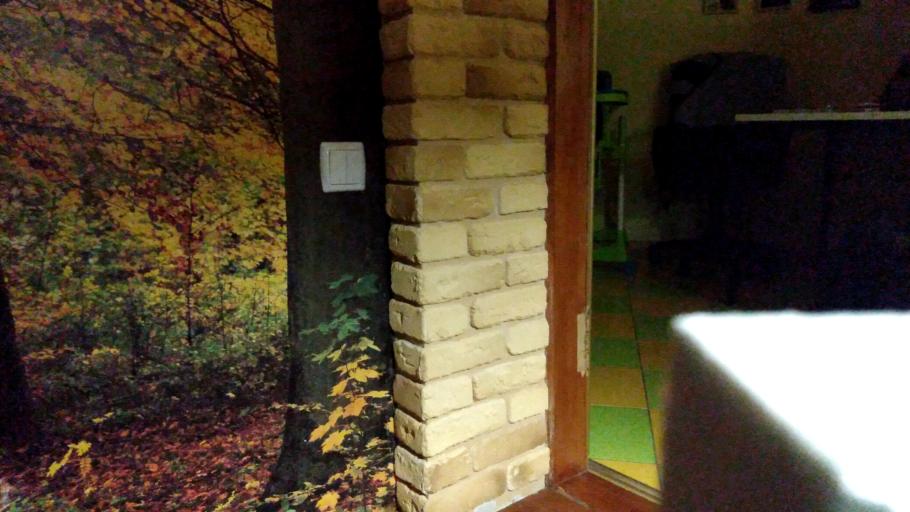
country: RU
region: Vologda
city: Lipin Bor
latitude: 60.9564
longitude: 37.9766
